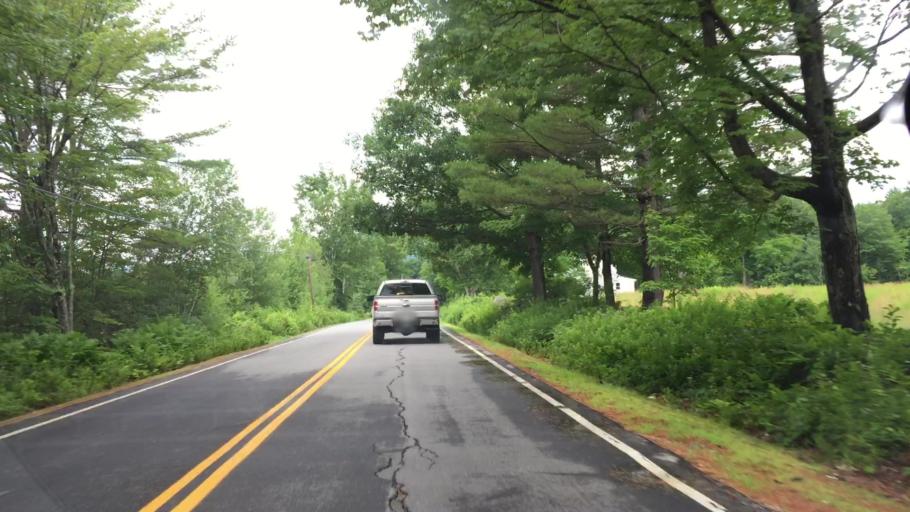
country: US
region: New Hampshire
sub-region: Carroll County
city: Sandwich
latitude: 43.8049
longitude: -71.4558
